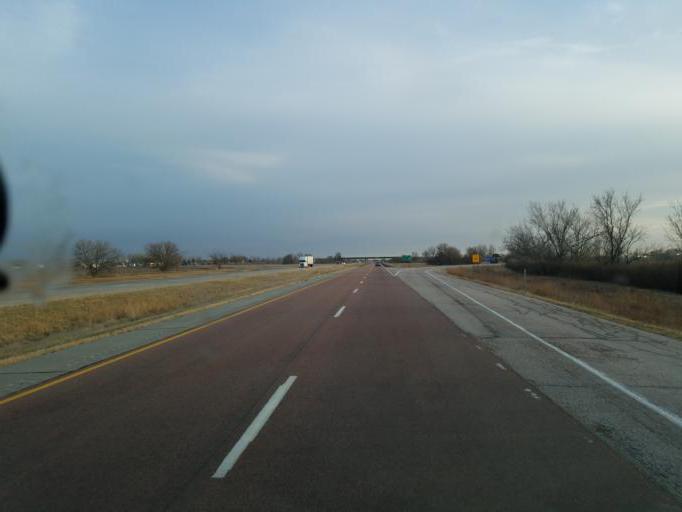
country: US
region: Iowa
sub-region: Monona County
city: Onawa
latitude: 42.0313
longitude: -96.1363
